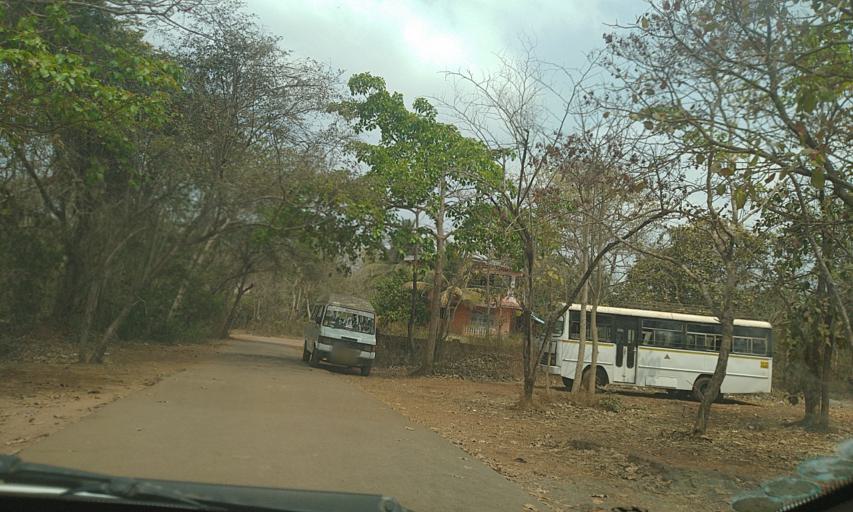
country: IN
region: Goa
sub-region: North Goa
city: Serula
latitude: 15.5394
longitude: 73.8248
